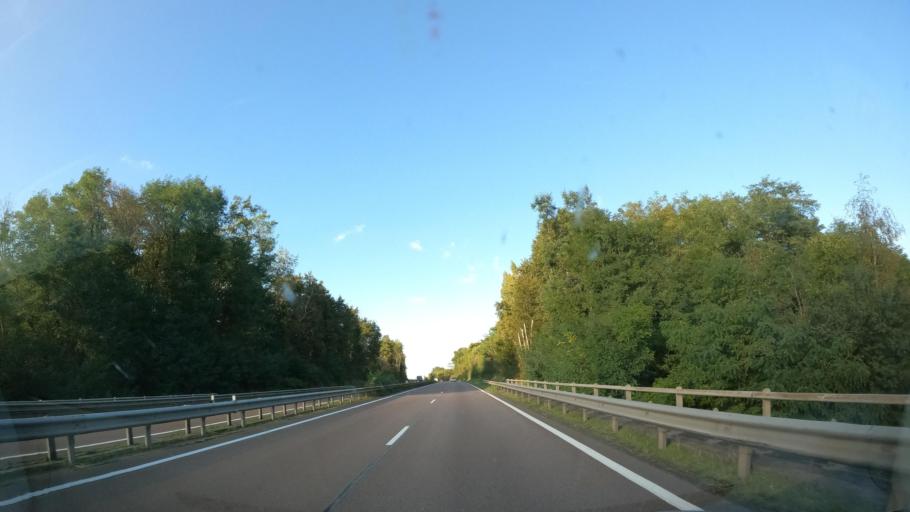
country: FR
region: Bourgogne
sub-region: Departement de Saone-et-Loire
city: Montceau-les-Mines
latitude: 46.6528
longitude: 4.3299
